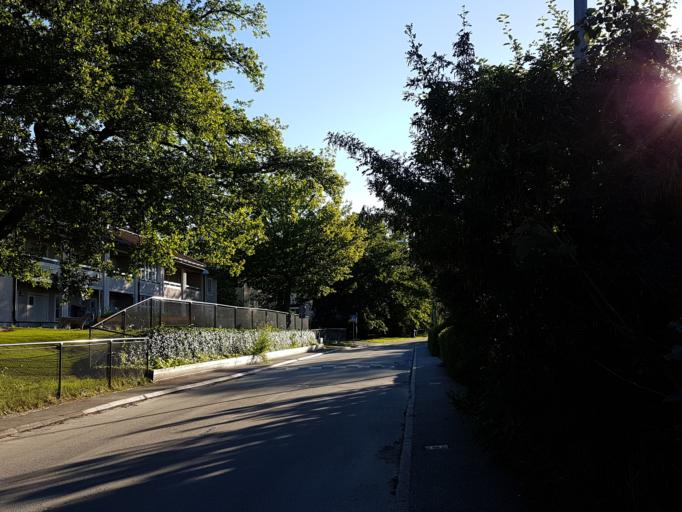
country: SE
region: Stockholm
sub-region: Stockholms Kommun
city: Bromma
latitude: 59.3250
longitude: 17.9694
